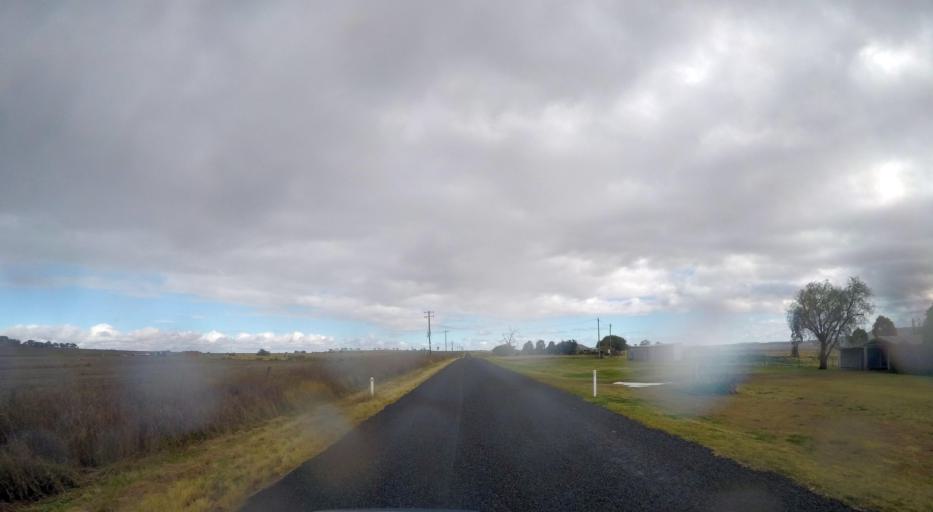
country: AU
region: Queensland
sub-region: Southern Downs
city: Warwick
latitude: -28.0512
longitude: 152.0339
